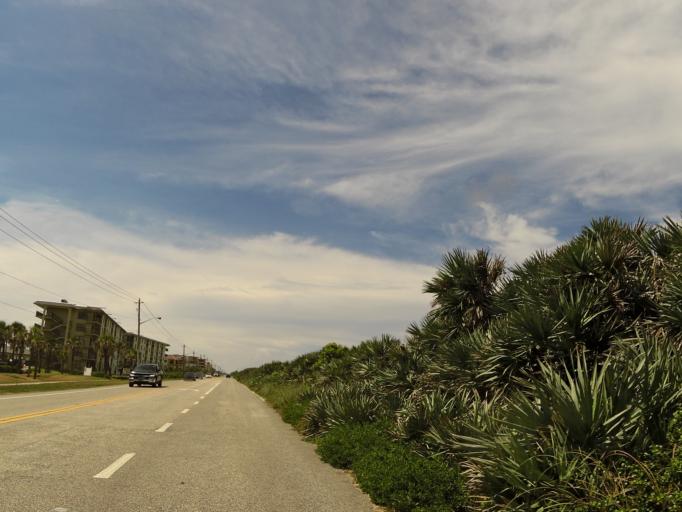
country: US
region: Florida
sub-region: Volusia County
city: Ormond-by-the-Sea
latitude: 29.3714
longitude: -81.0772
